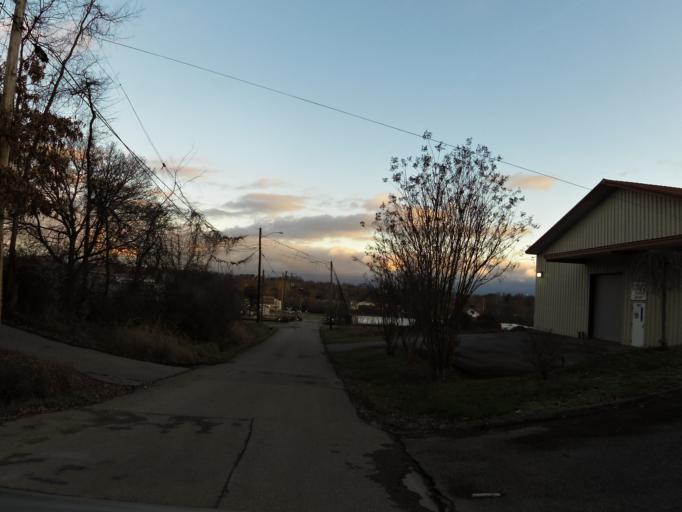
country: US
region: Tennessee
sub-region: Knox County
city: Knoxville
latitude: 36.0116
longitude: -83.9270
